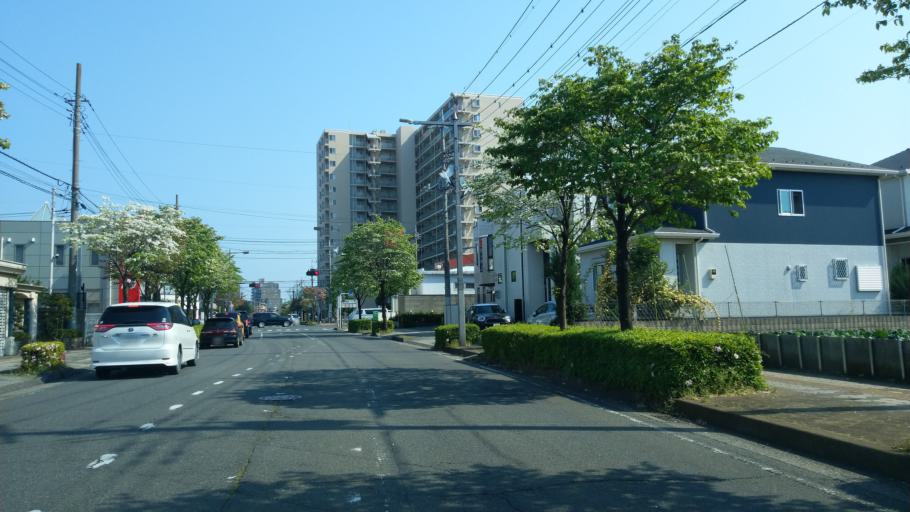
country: JP
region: Saitama
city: Oi
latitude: 35.8569
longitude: 139.5198
